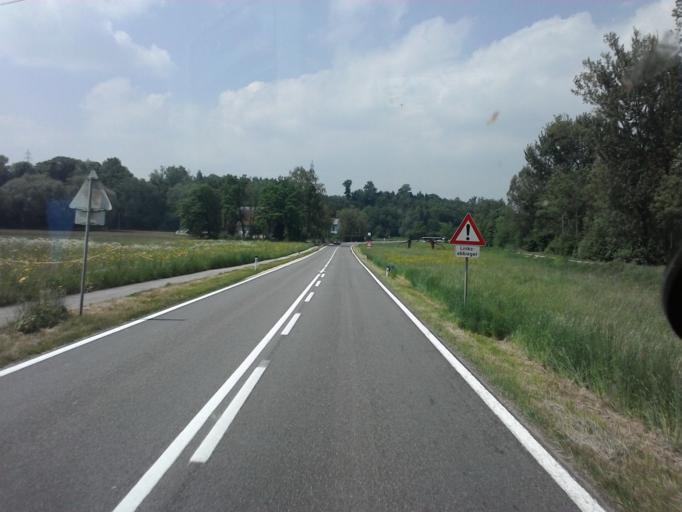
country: AT
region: Upper Austria
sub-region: Politischer Bezirk Steyr-Land
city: Bad Hall
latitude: 48.0463
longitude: 14.2069
